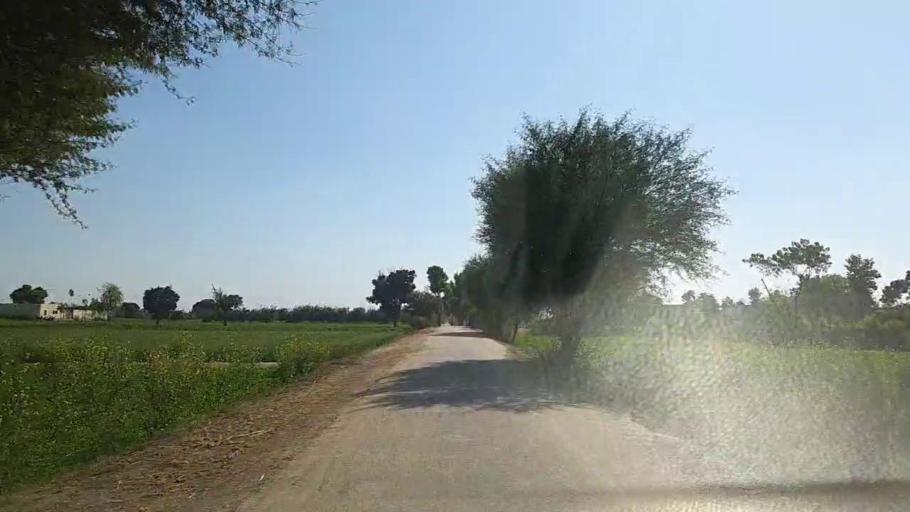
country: PK
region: Sindh
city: Nawabshah
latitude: 26.2354
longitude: 68.4457
